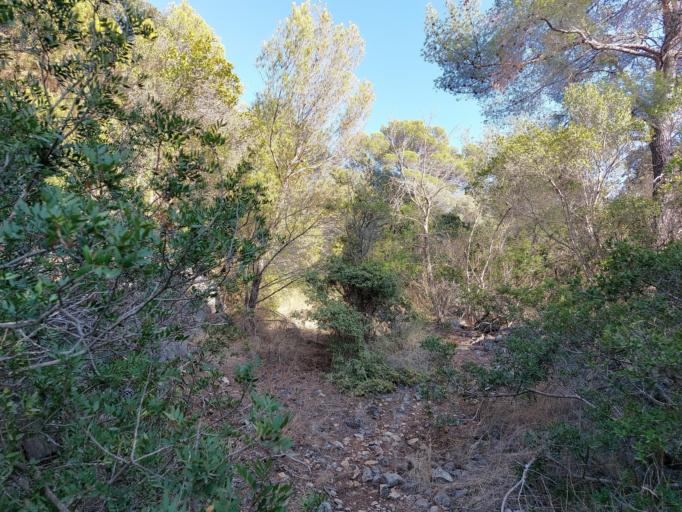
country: HR
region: Dubrovacko-Neretvanska
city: Smokvica
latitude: 42.7550
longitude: 16.8116
